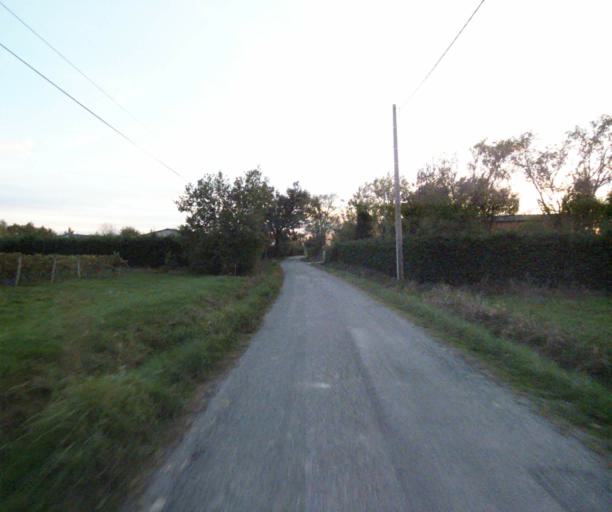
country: FR
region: Midi-Pyrenees
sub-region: Departement du Tarn-et-Garonne
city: Campsas
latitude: 43.9281
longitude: 1.3293
